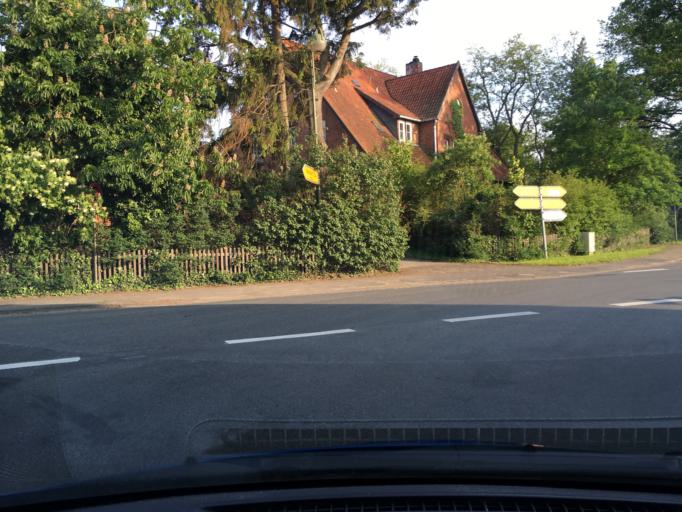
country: DE
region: Lower Saxony
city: Scharnebeck
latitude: 53.2935
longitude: 10.5080
